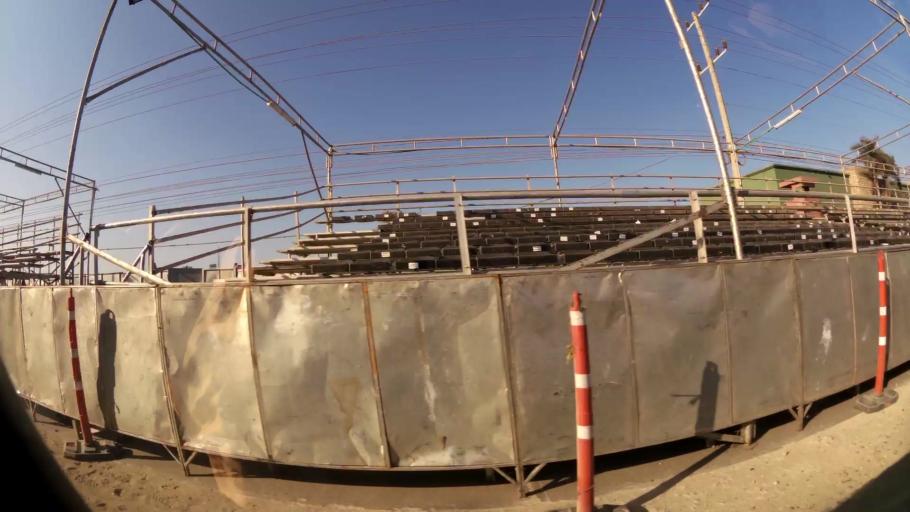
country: CO
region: Atlantico
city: Barranquilla
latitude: 11.0196
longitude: -74.7981
